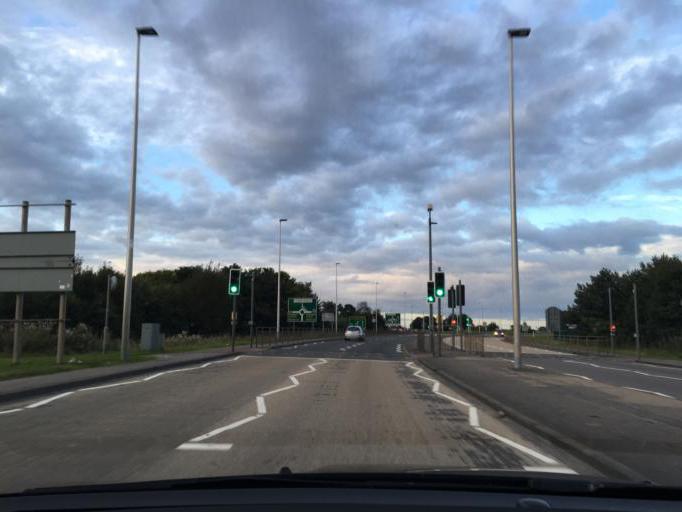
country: GB
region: Scotland
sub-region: Highland
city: Inverness
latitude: 57.4901
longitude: -4.2180
